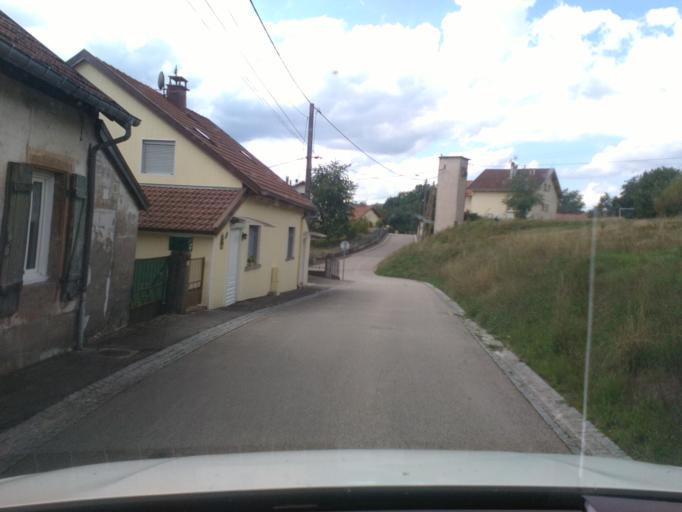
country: FR
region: Lorraine
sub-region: Departement des Vosges
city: Moyenmoutier
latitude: 48.3791
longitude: 6.9077
